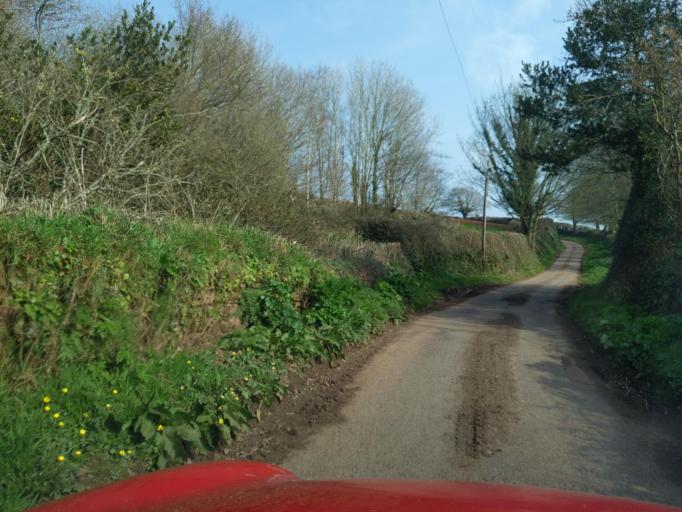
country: GB
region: England
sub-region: Devon
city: Kingsbridge
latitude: 50.2859
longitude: -3.7246
